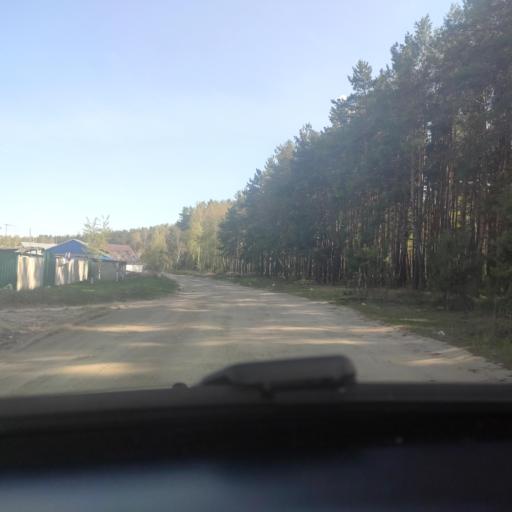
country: RU
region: Voronezj
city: Somovo
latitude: 51.7517
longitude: 39.3223
